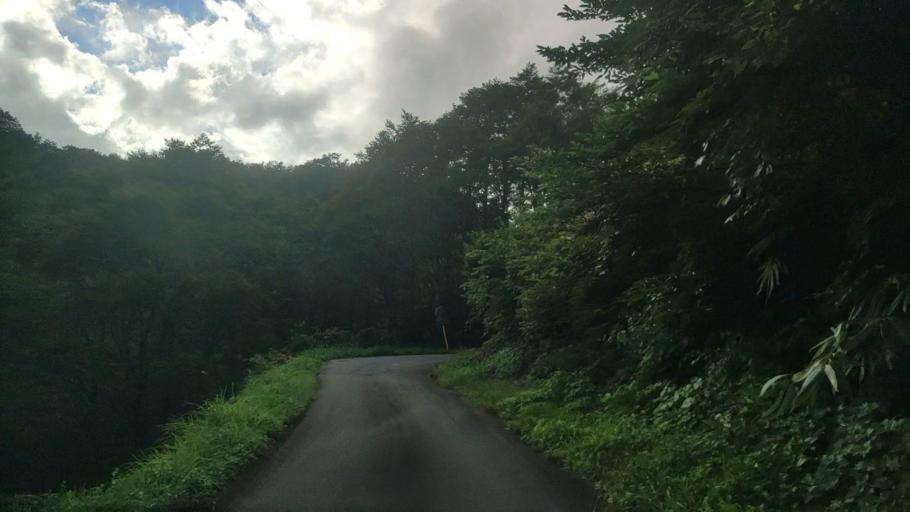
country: JP
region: Toyama
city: Yatsuomachi-higashikumisaka
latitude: 36.3465
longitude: 137.0690
